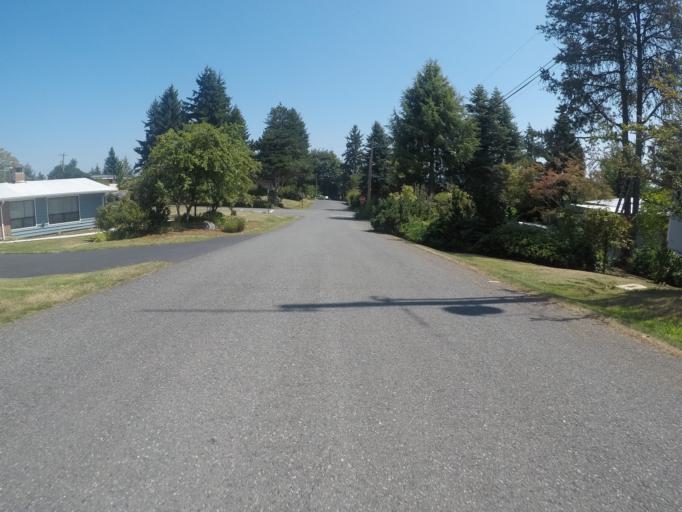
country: US
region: Washington
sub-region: King County
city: Kenmore
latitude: 47.7644
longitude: -122.2579
